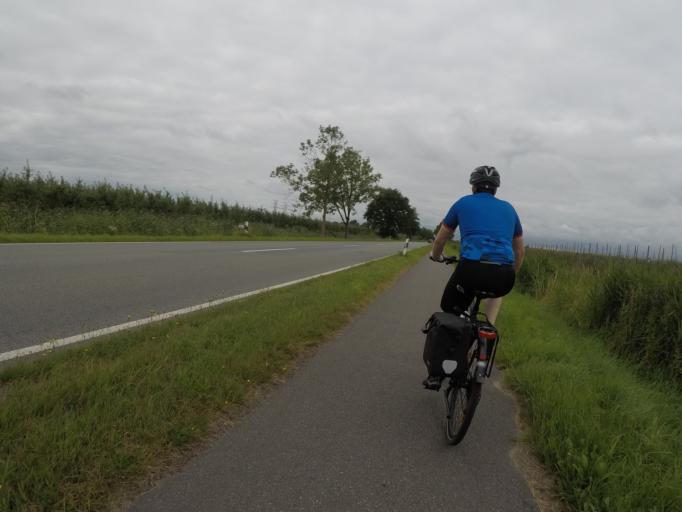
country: DE
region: Lower Saxony
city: Mittelnkirchen
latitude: 53.5394
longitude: 9.6410
